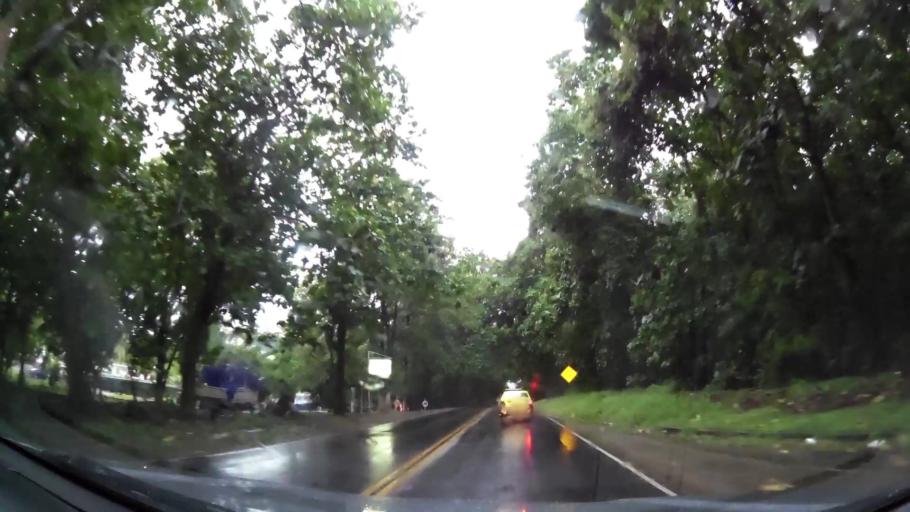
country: PA
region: Panama
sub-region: Distrito de Panama
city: Paraiso
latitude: 9.0144
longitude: -79.6009
